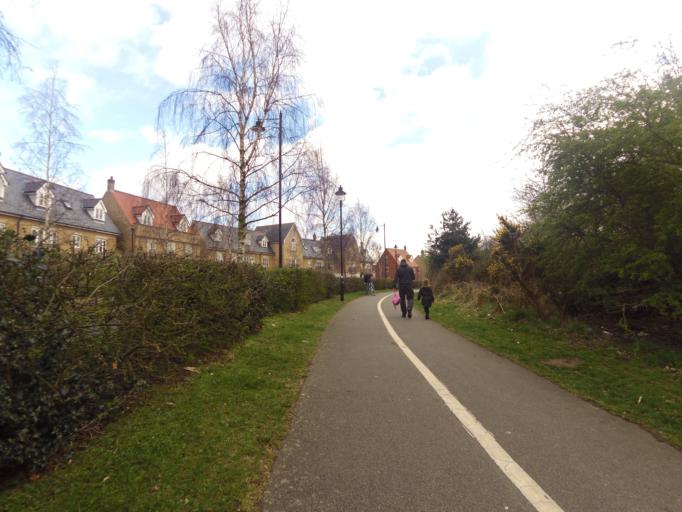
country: GB
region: England
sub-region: Suffolk
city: Ipswich
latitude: 52.0323
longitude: 1.1916
